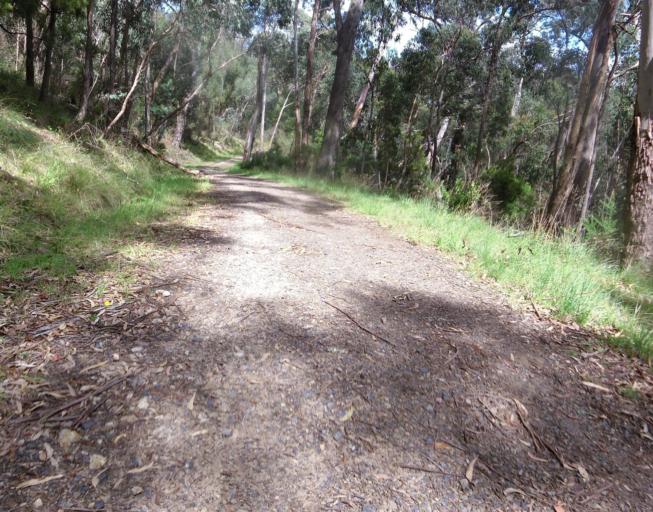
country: AU
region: Victoria
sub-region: Yarra Ranges
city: Montrose
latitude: -37.8271
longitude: 145.3437
